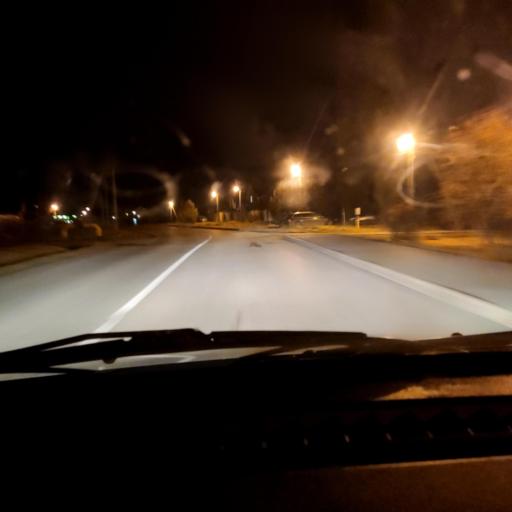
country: RU
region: Bashkortostan
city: Avdon
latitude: 54.6959
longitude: 55.7961
